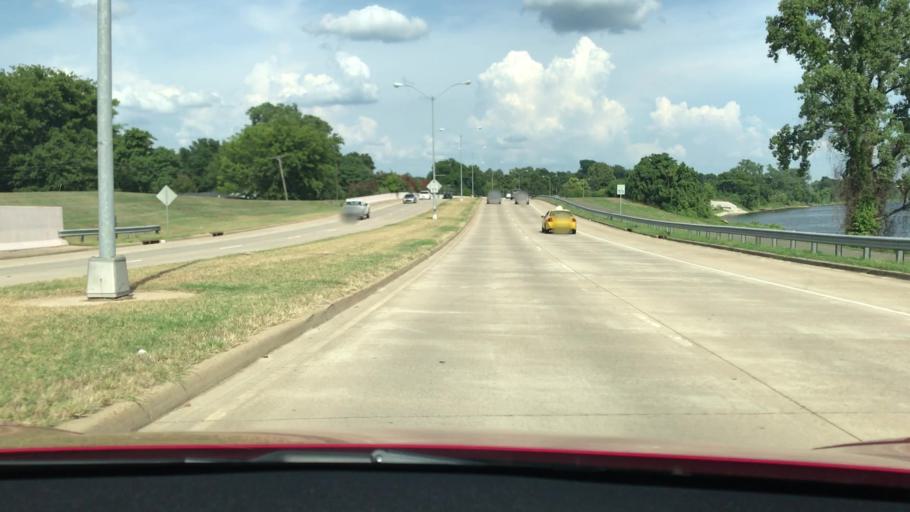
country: US
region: Louisiana
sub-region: Bossier Parish
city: Bossier City
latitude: 32.5100
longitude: -93.7201
